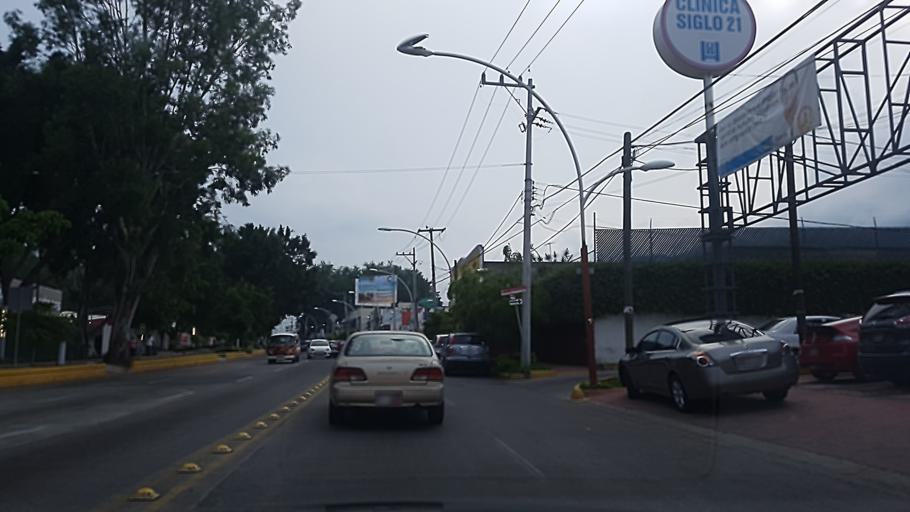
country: MX
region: Nayarit
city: Tepic
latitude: 21.5067
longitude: -104.9011
